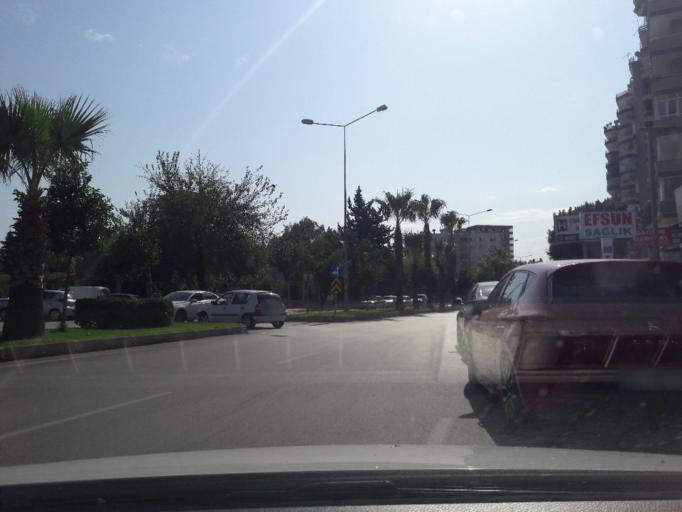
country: TR
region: Adana
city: Adana
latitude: 37.0187
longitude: 35.3209
